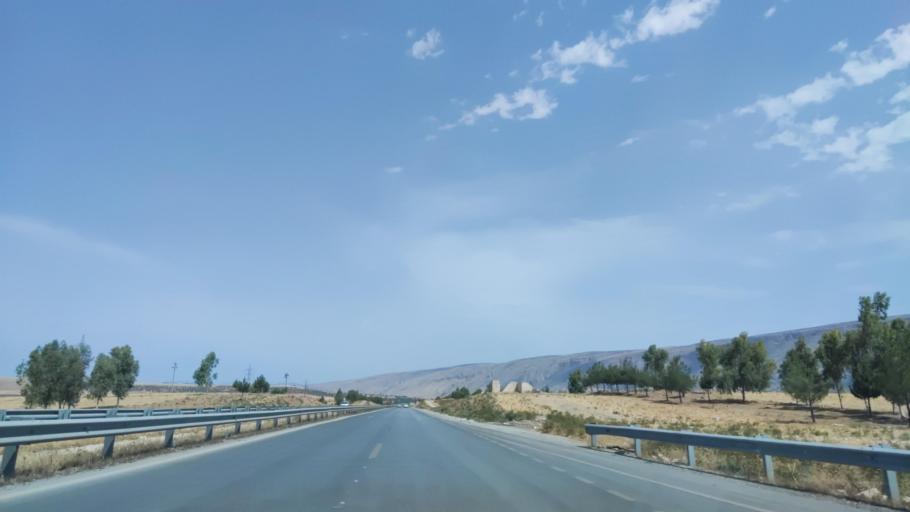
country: IQ
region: Arbil
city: Shaqlawah
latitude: 36.4610
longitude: 44.3838
